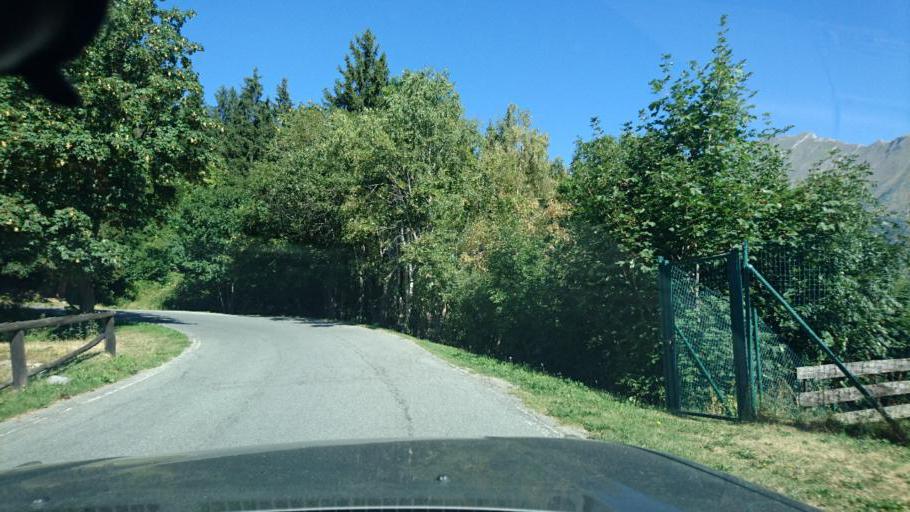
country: IT
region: Aosta Valley
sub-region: Valle d'Aosta
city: Morgex
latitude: 45.7518
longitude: 7.0213
